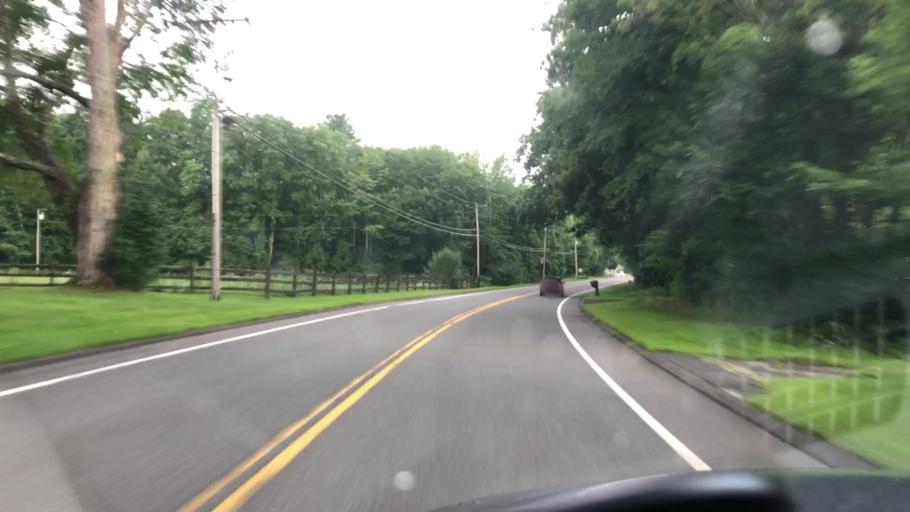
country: US
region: Massachusetts
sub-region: Hampshire County
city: Westhampton
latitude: 42.2868
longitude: -72.7514
